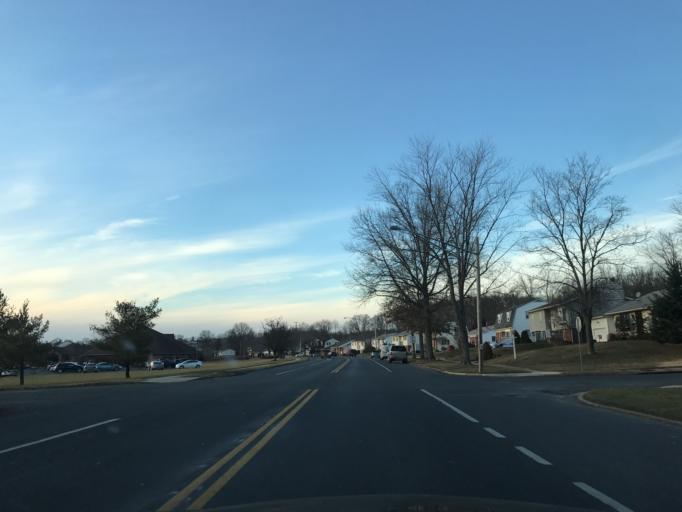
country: US
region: Maryland
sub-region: Harford County
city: Joppatowne
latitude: 39.4098
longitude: -76.3499
